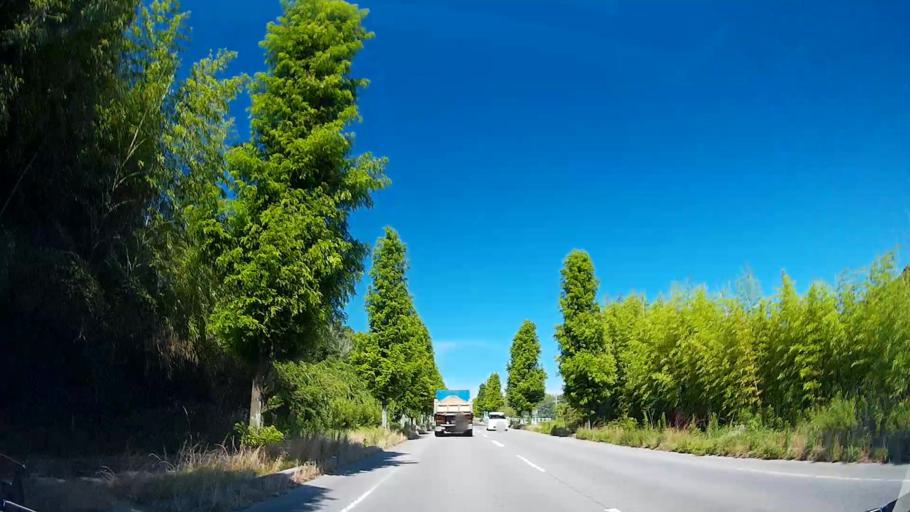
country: JP
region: Aichi
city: Gamagori
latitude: 34.8312
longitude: 137.1598
